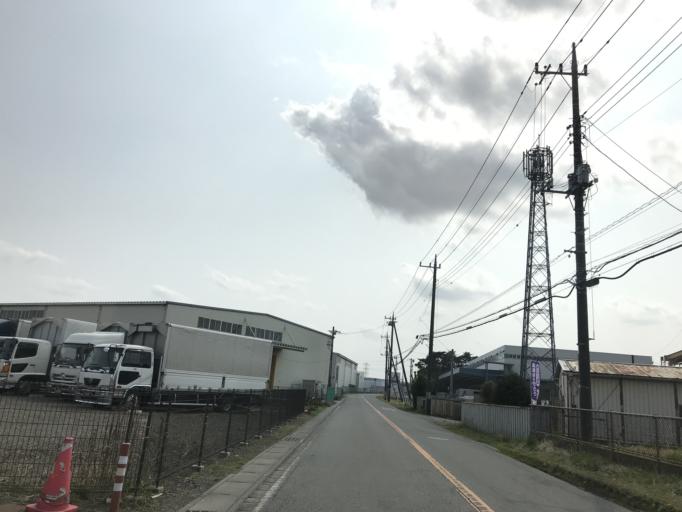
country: JP
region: Ibaraki
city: Ushiku
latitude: 35.9998
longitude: 140.0696
